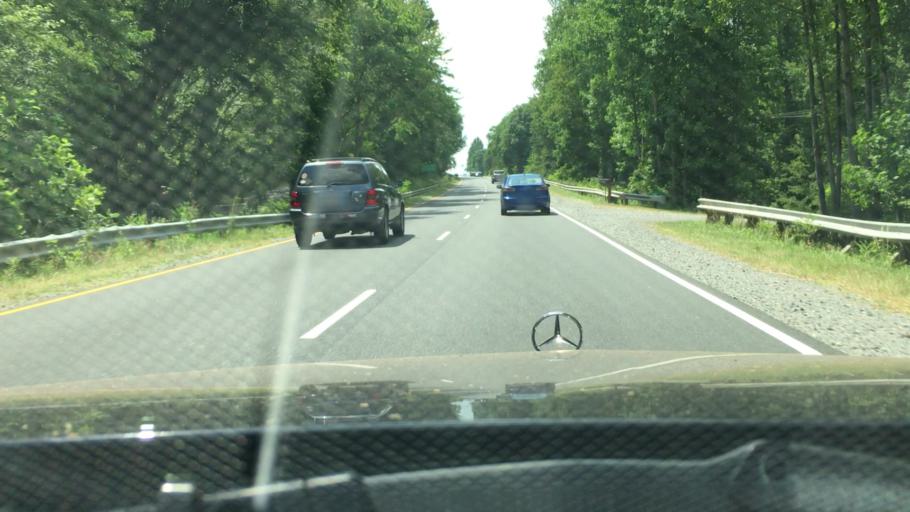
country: US
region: Virginia
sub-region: Spotsylvania County
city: Spotsylvania
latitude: 38.3221
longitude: -77.7040
